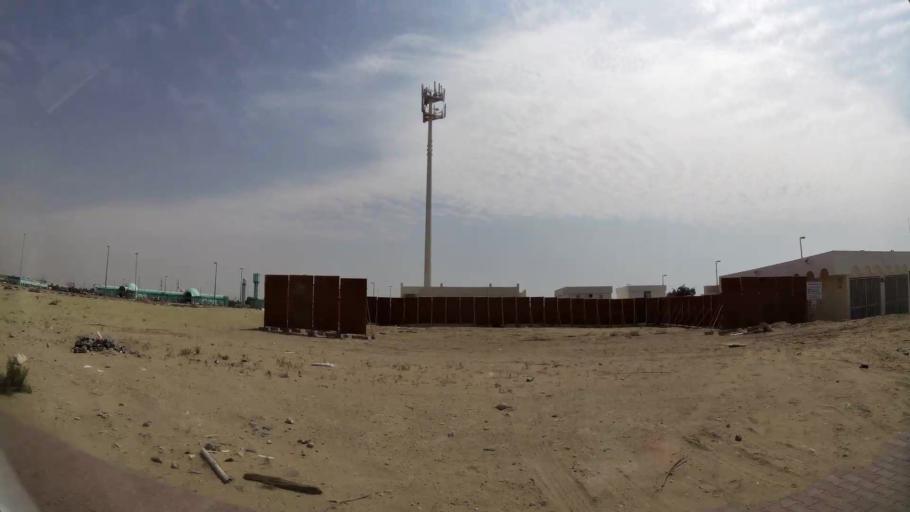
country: AE
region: Abu Dhabi
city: Abu Dhabi
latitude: 24.5456
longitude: 54.6830
